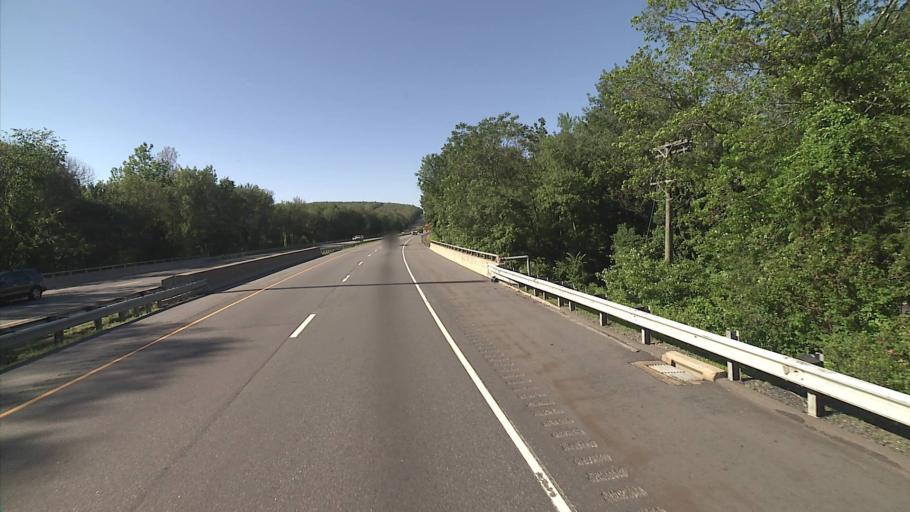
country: US
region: Connecticut
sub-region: New London County
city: Oxoboxo River
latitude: 41.4610
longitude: -72.1153
